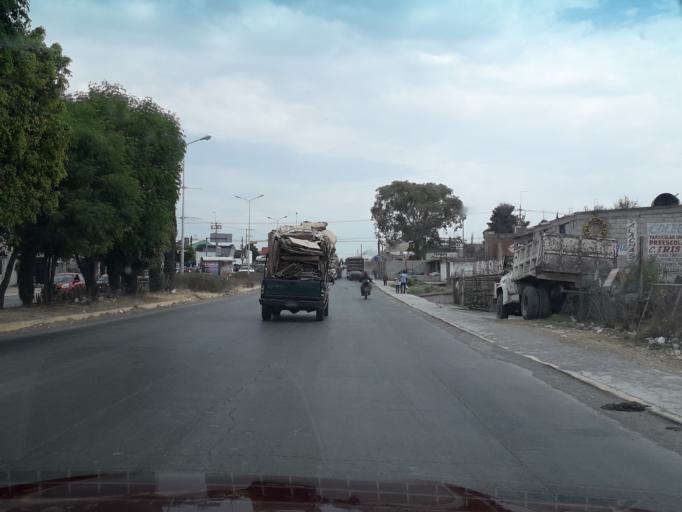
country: MX
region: Puebla
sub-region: Puebla
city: El Capulo (La Quebradora)
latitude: 18.9662
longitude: -98.2673
